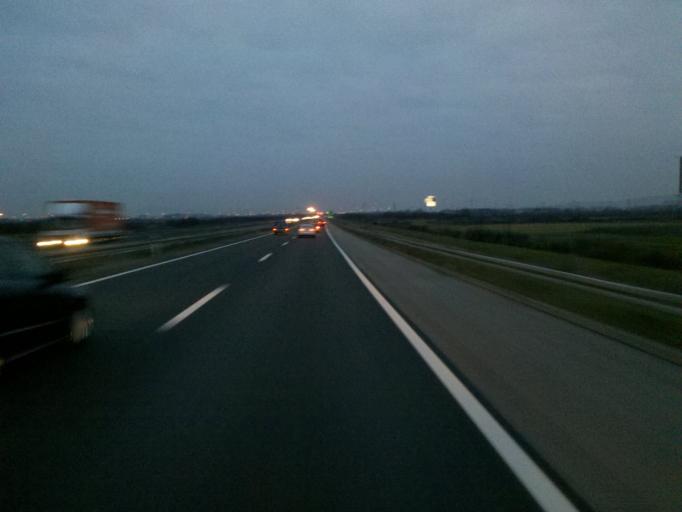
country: HR
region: Zagrebacka
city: Micevec
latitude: 45.7472
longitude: 16.0329
